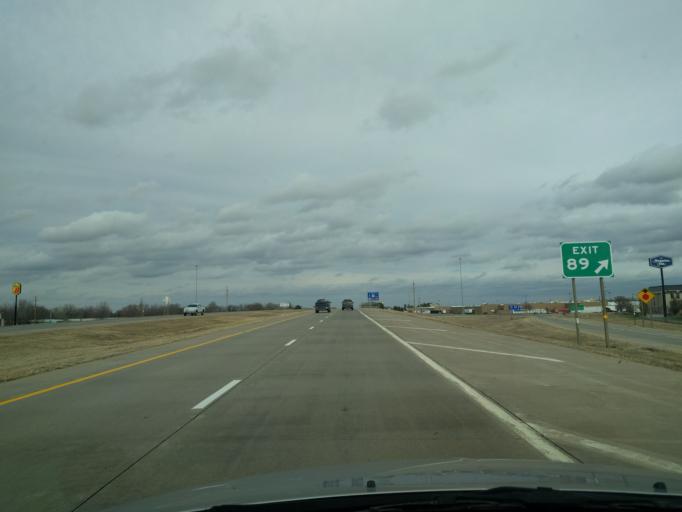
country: US
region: Kansas
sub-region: Saline County
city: Salina
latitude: 38.7812
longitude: -97.6168
